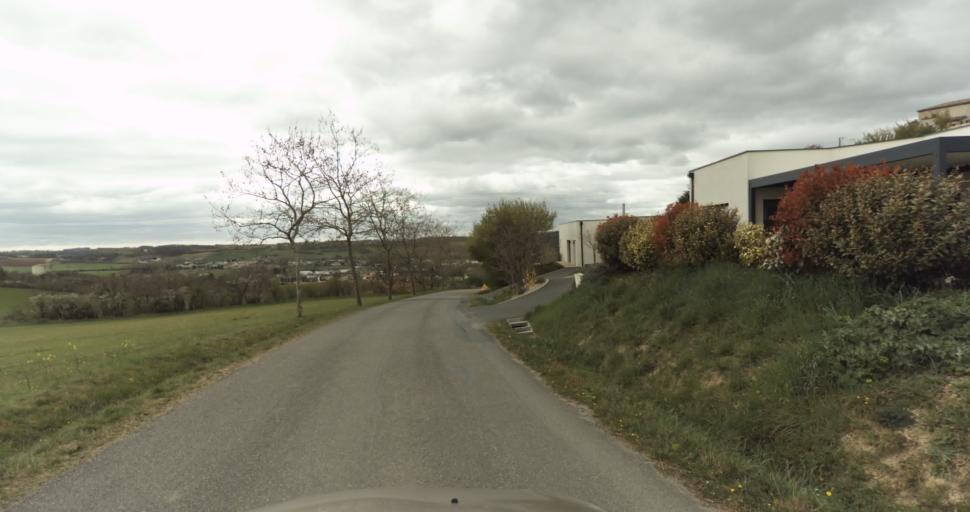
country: FR
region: Midi-Pyrenees
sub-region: Departement du Tarn
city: Puygouzon
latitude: 43.8987
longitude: 2.1694
